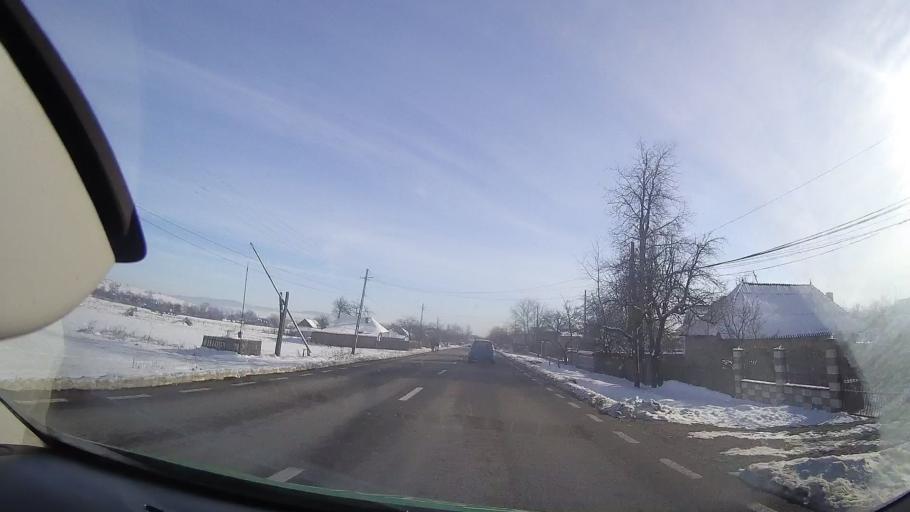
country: RO
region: Neamt
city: Bodesti
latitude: 47.0548
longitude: 26.3965
